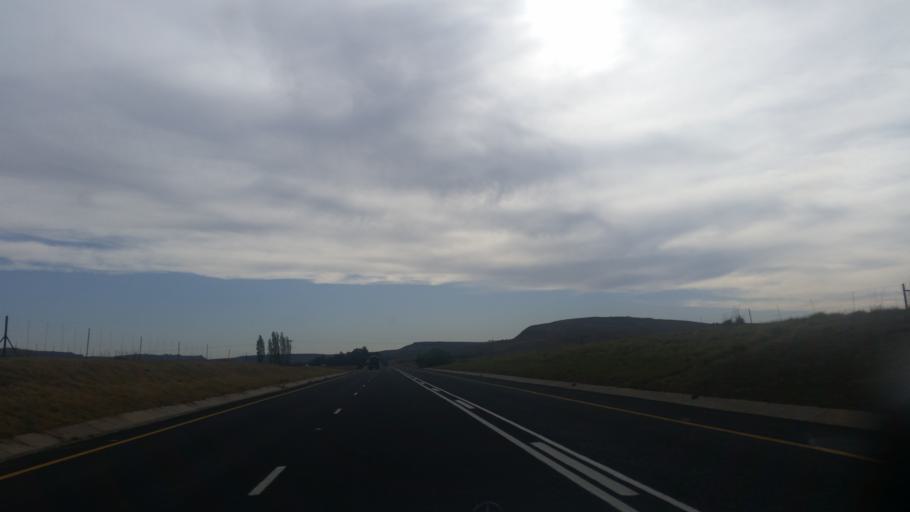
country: ZA
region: Orange Free State
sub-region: Thabo Mofutsanyana District Municipality
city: Phuthaditjhaba
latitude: -28.3128
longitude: 28.7415
